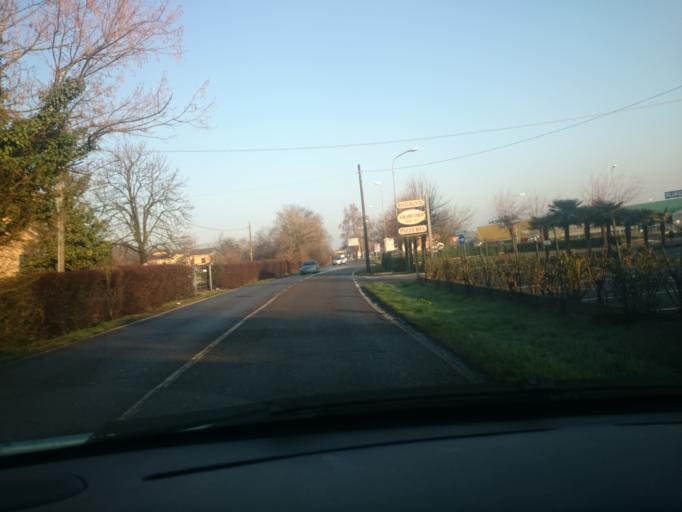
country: IT
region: Emilia-Romagna
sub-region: Provincia di Reggio Emilia
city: Fogliano
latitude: 44.6674
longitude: 10.6421
